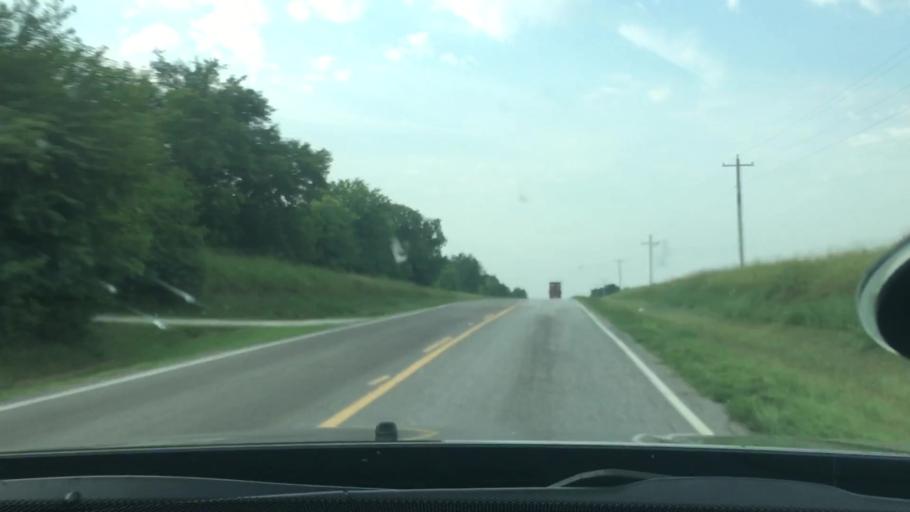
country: US
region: Oklahoma
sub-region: Coal County
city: Coalgate
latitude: 34.4124
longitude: -96.4246
